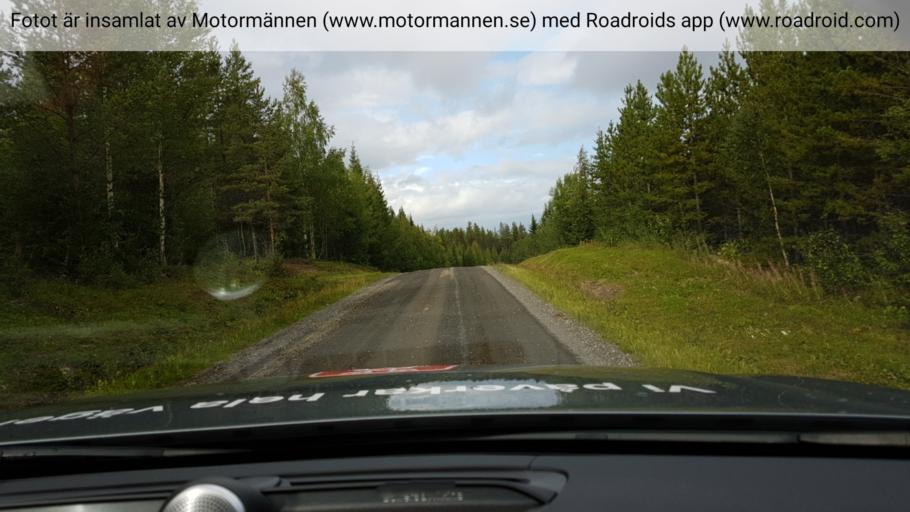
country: SE
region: Jaemtland
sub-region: OEstersunds Kommun
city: Lit
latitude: 63.7523
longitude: 14.6531
